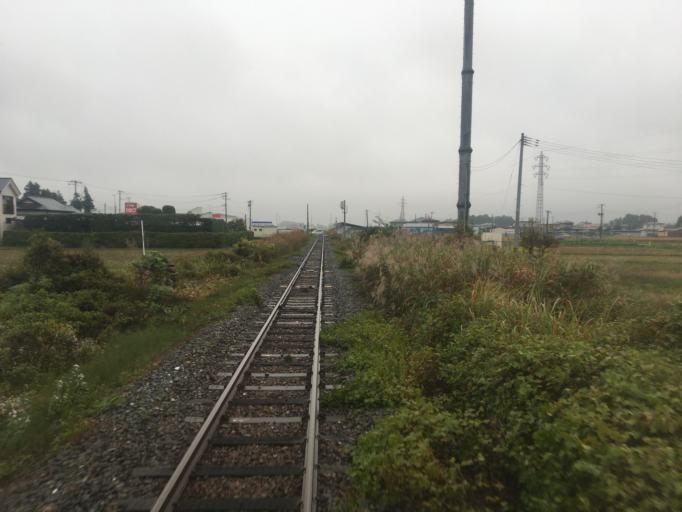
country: JP
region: Miyagi
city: Kogota
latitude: 38.5594
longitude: 141.0255
